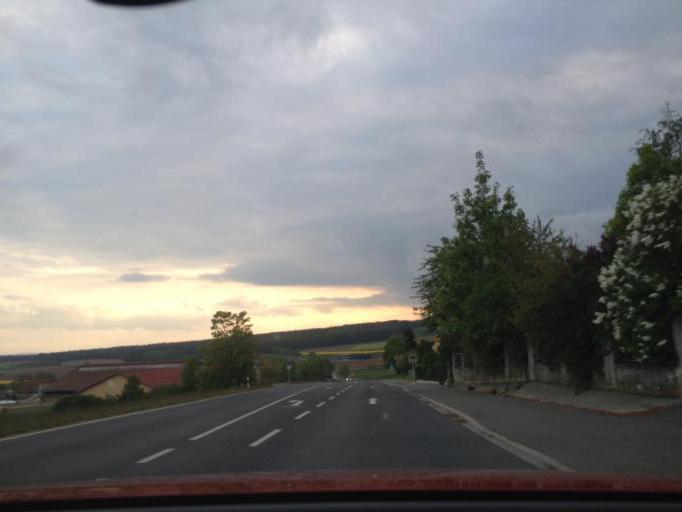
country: DE
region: Bavaria
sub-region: Upper Palatinate
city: Gebenbach
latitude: 49.5366
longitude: 11.8669
